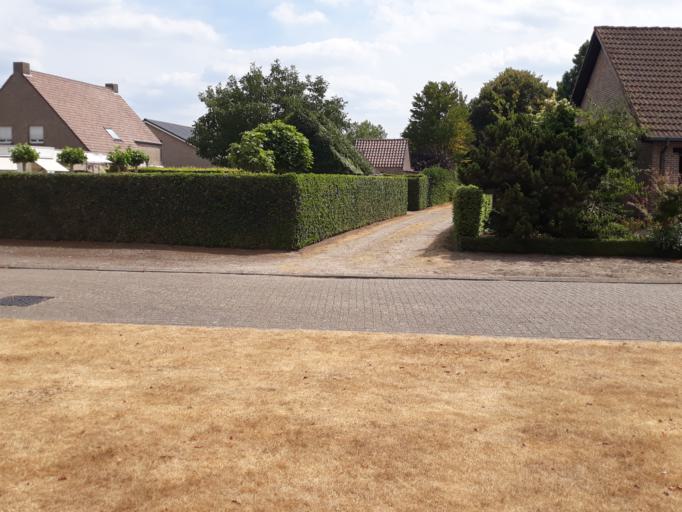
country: NL
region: North Brabant
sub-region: Gemeente Goirle
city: Goirle
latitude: 51.4448
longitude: 5.0427
